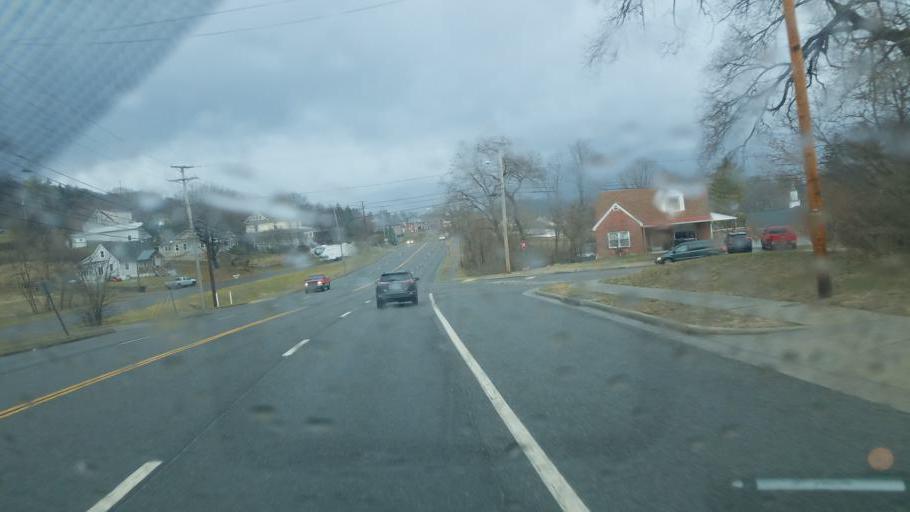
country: US
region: Virginia
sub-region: Giles County
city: Pearisburg
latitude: 37.3218
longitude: -80.7306
